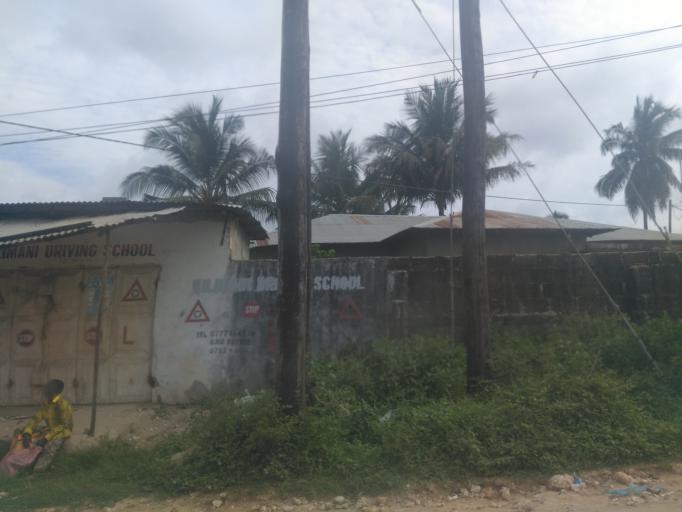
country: TZ
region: Zanzibar Urban/West
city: Zanzibar
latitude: -6.1791
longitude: 39.2172
